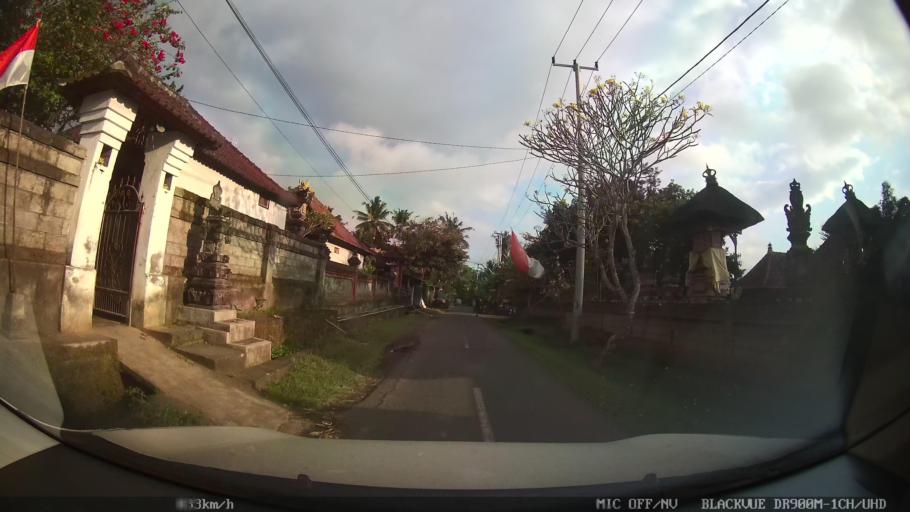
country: ID
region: Bali
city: Banjar Tebongkang
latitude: -8.5376
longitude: 115.2521
